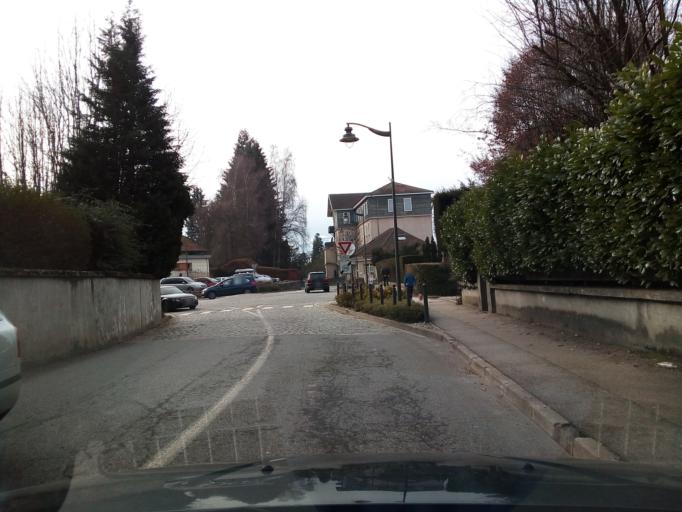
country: FR
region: Rhone-Alpes
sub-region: Departement de l'Isere
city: Vaulnaveys-le-Haut
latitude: 45.1513
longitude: 5.8372
